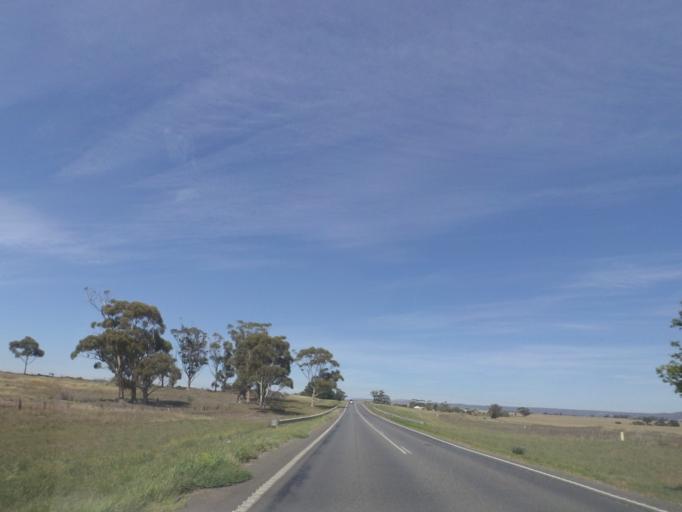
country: AU
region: Victoria
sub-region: Moorabool
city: Bacchus Marsh
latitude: -37.7964
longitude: 144.4122
